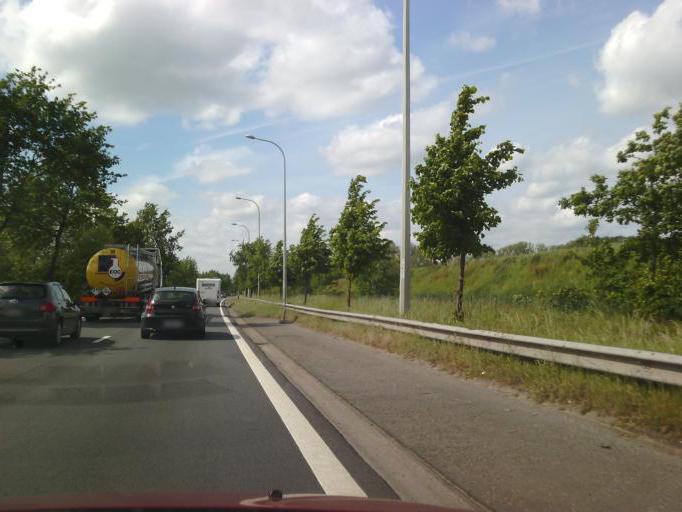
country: BE
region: Flanders
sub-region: Provincie Oost-Vlaanderen
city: Gent
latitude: 51.0579
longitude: 3.6663
